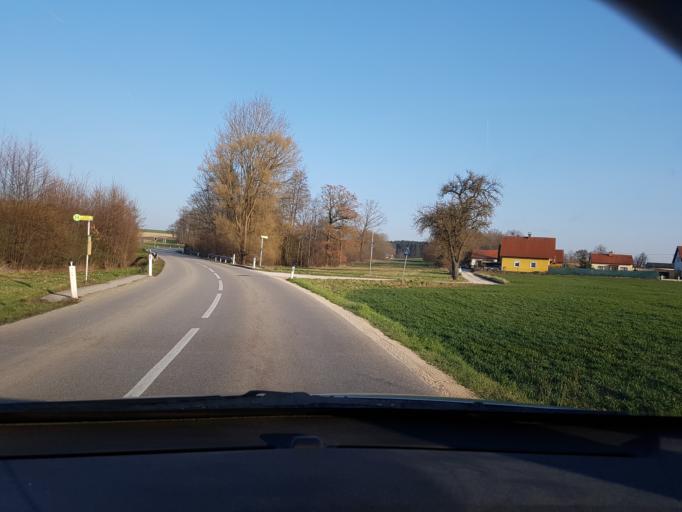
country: AT
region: Upper Austria
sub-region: Politischer Bezirk Linz-Land
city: Ansfelden
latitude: 48.1580
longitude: 14.2500
